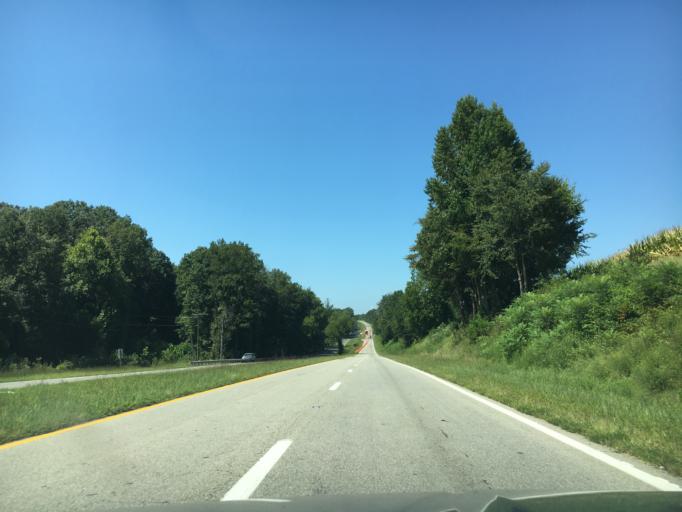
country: US
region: Virginia
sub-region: City of Danville
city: Danville
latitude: 36.5812
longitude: -79.1944
